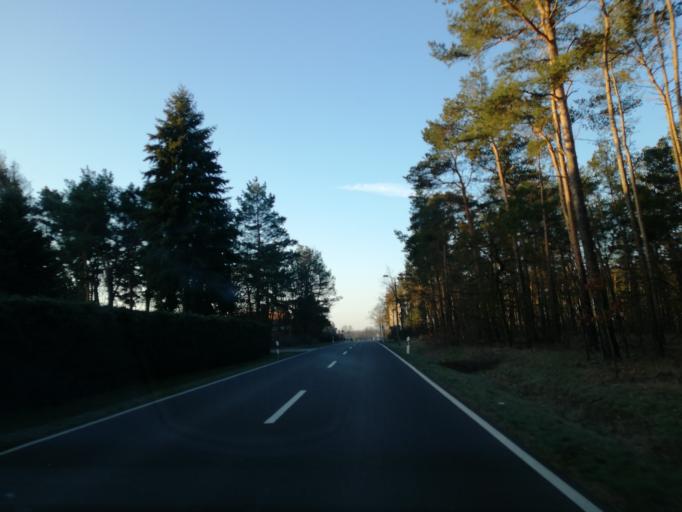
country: DE
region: Brandenburg
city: Finsterwalde
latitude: 51.6518
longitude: 13.7102
